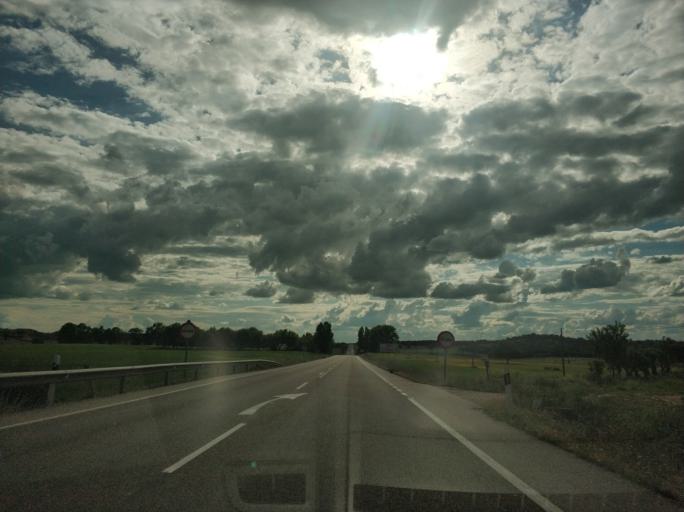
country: ES
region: Castille and Leon
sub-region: Provincia de Burgos
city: Valdezate
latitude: 41.6142
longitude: -3.9323
